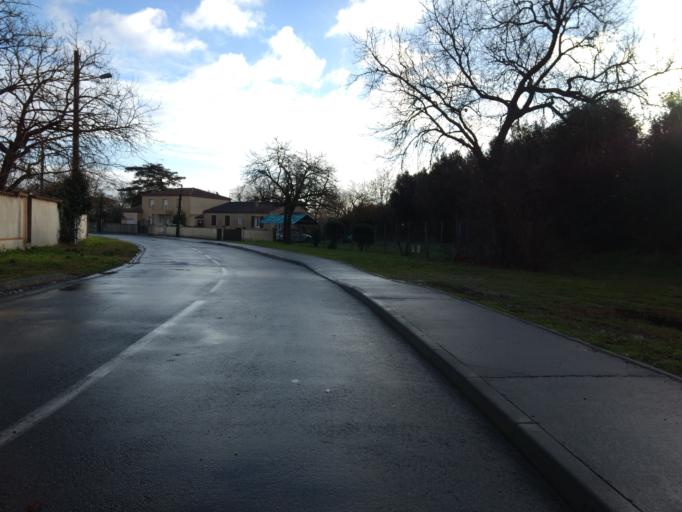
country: FR
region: Midi-Pyrenees
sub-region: Departement de la Haute-Garonne
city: Tournefeuille
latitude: 43.6069
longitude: 1.3136
